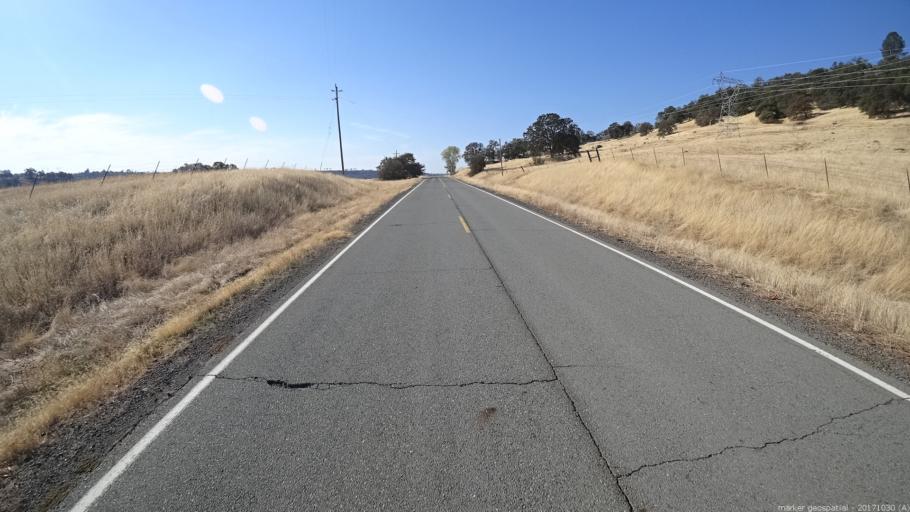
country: US
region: California
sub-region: Shasta County
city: Bella Vista
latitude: 40.6463
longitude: -122.0801
